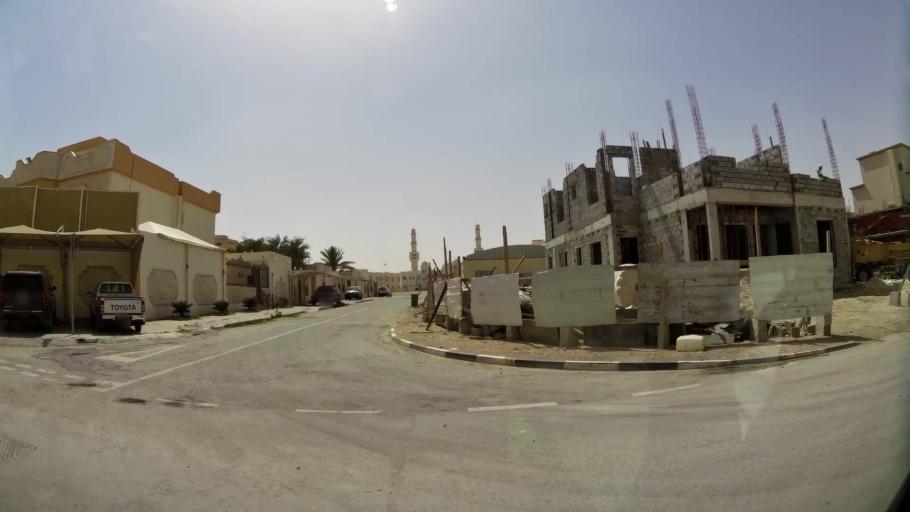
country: QA
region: Baladiyat Umm Salal
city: Umm Salal Muhammad
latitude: 25.3931
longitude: 51.4179
